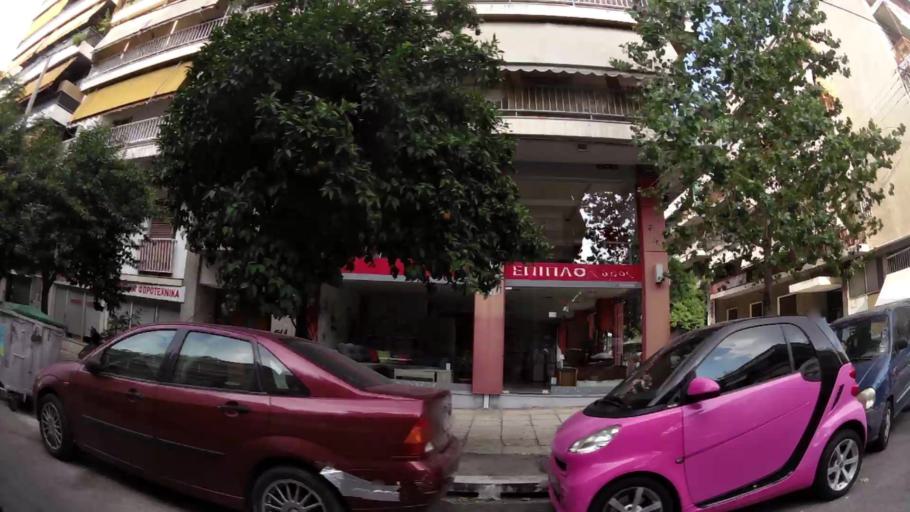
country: GR
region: Attica
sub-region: Nomarchia Athinas
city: Kallithea
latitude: 37.9496
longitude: 23.7039
